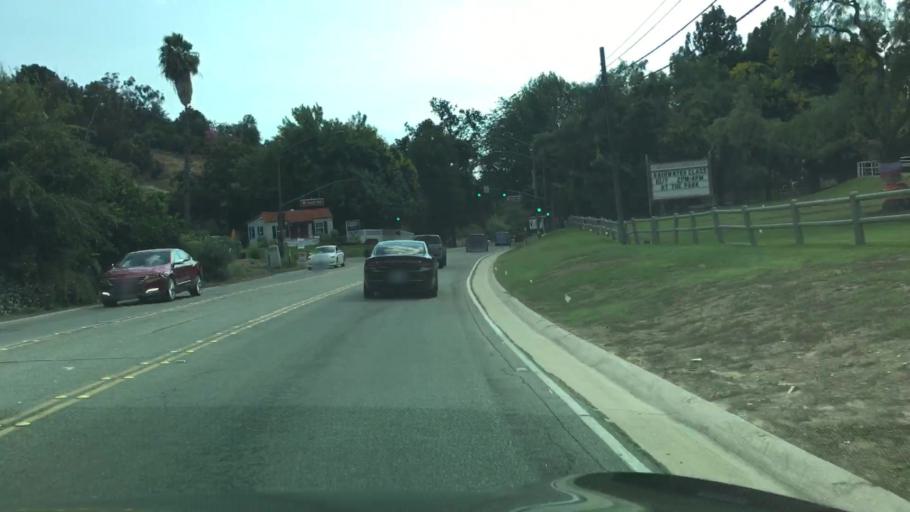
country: US
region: California
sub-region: Los Angeles County
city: La Habra Heights
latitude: 33.9567
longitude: -117.9579
